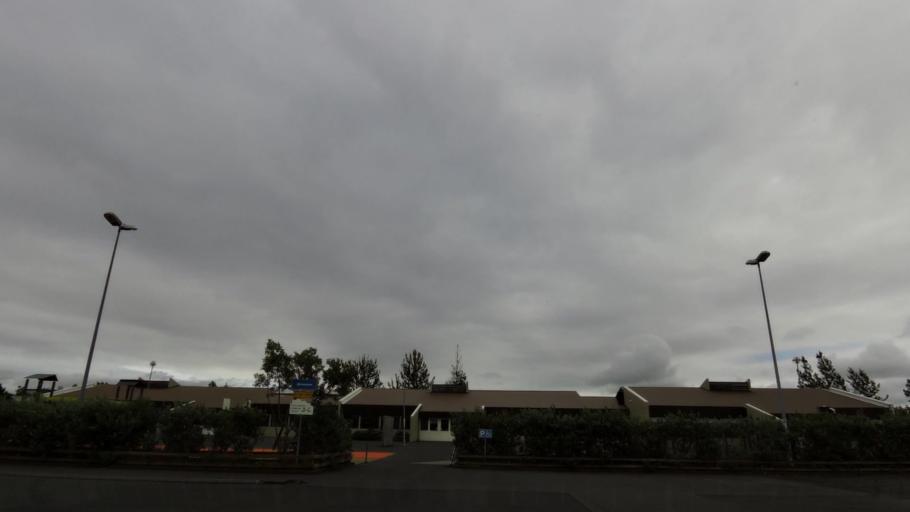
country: IS
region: Capital Region
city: Hafnarfjoerdur
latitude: 64.0817
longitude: -21.9581
